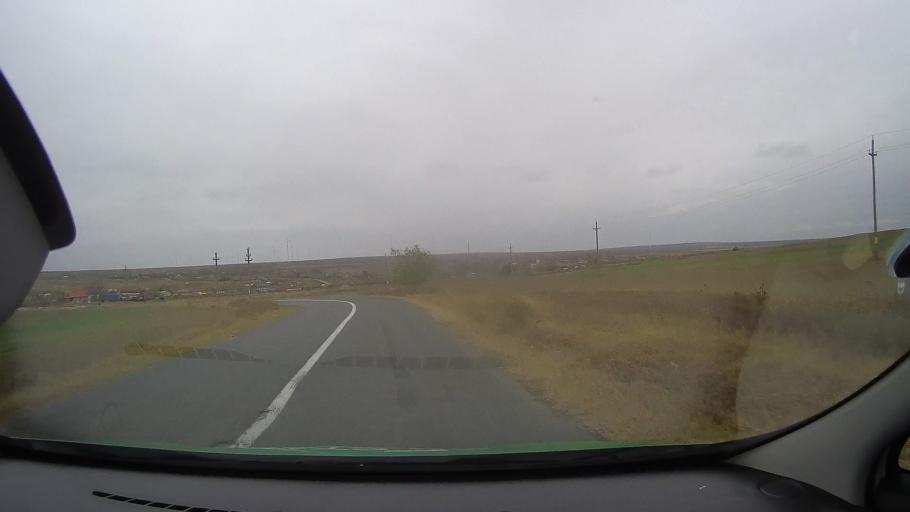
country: RO
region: Constanta
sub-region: Comuna Targusor
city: Targusor
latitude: 44.4885
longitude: 28.3644
